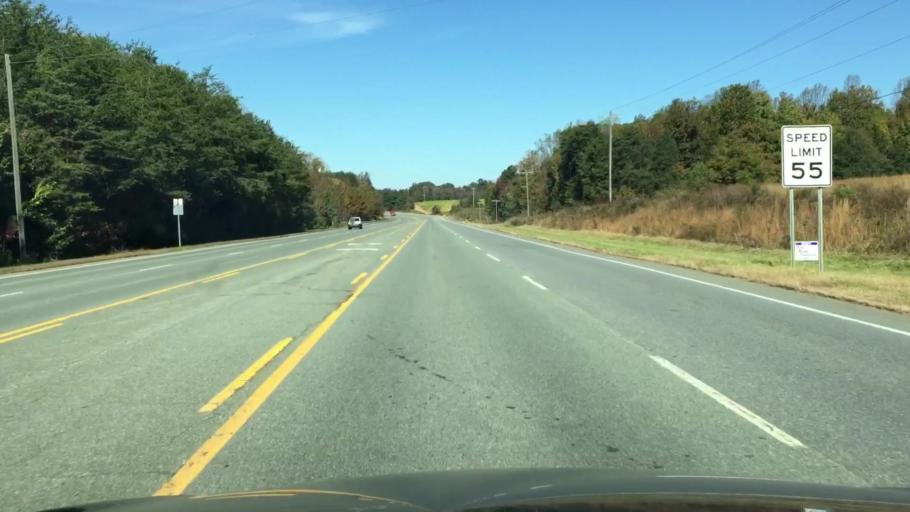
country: US
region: North Carolina
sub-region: Rockingham County
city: Reidsville
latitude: 36.3159
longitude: -79.6317
